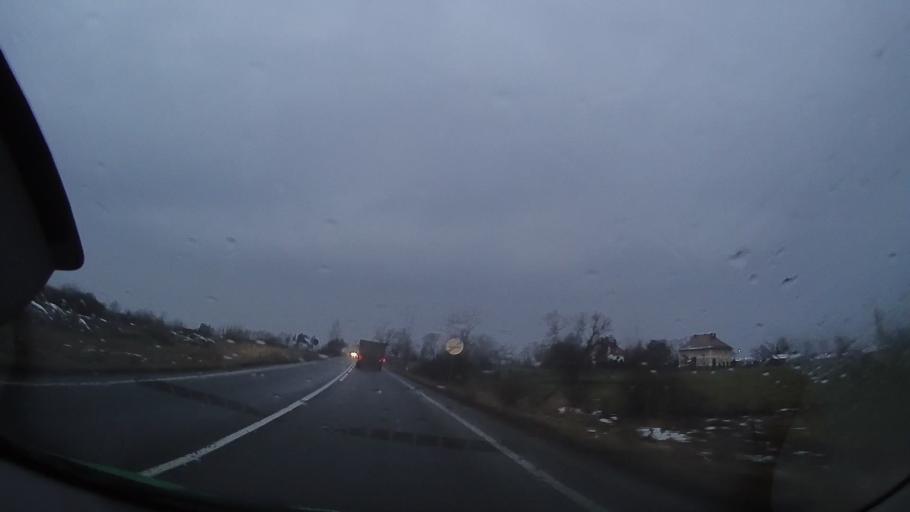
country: RO
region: Harghita
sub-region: Comuna Lazarea
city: Lazarea
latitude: 46.7645
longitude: 25.5140
